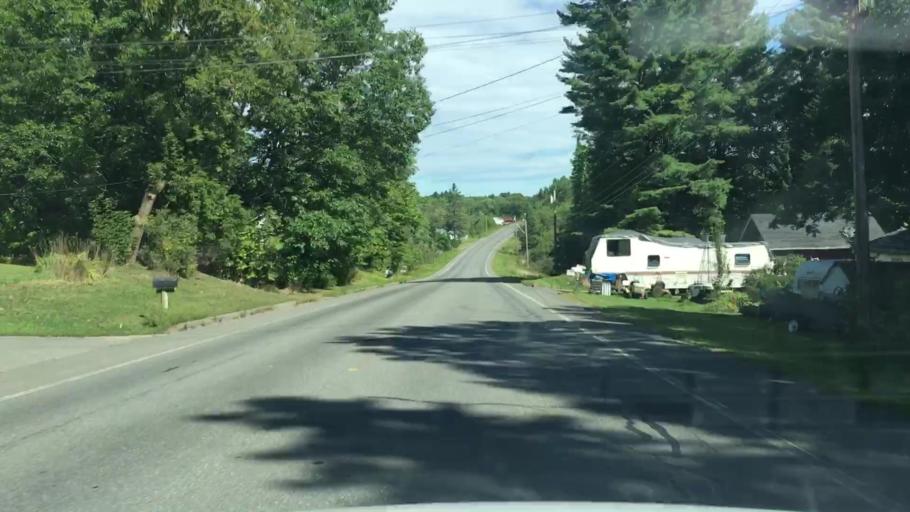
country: US
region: Maine
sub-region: Penobscot County
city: Dexter
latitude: 45.0786
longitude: -69.2306
